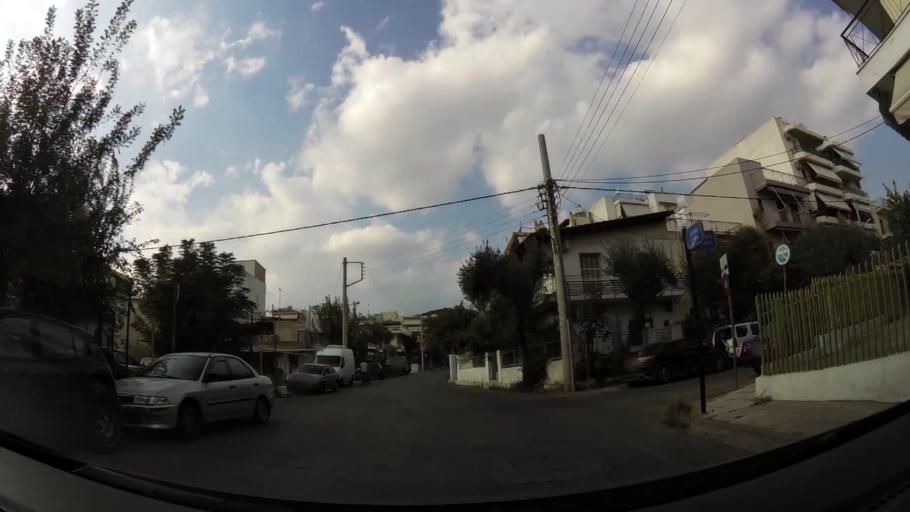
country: GR
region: Attica
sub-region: Nomarchia Athinas
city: Ilion
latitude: 38.0416
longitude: 23.6958
